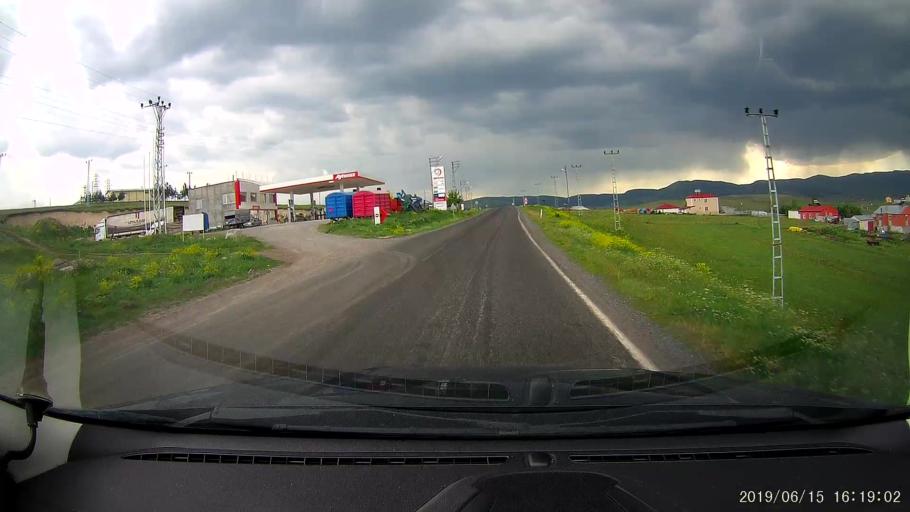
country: TR
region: Ardahan
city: Hanak
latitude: 41.2327
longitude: 42.8524
